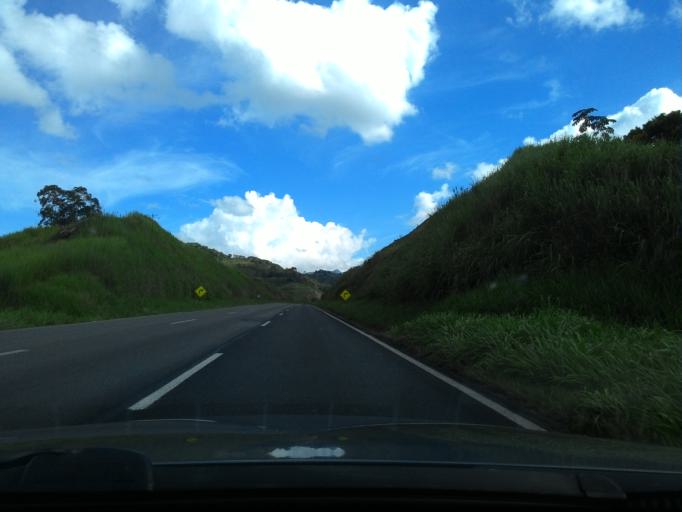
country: BR
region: Sao Paulo
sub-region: Cajati
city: Cajati
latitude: -24.7843
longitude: -48.2084
